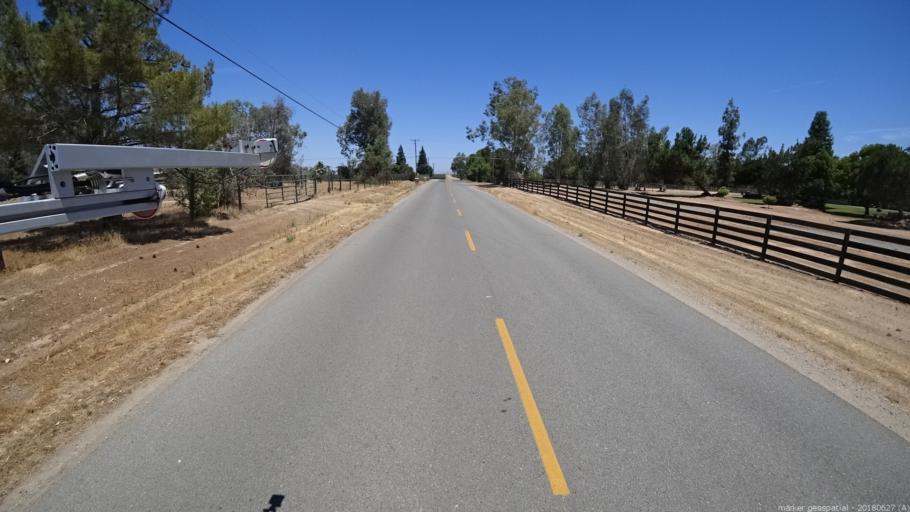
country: US
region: California
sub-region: Madera County
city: Bonadelle Ranchos-Madera Ranchos
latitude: 36.9349
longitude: -119.8625
